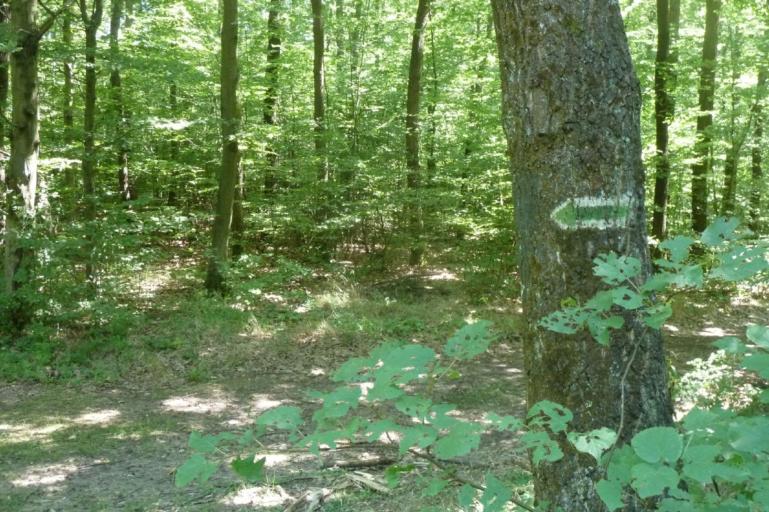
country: HU
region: Pest
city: Szob
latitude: 47.8927
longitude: 18.9199
